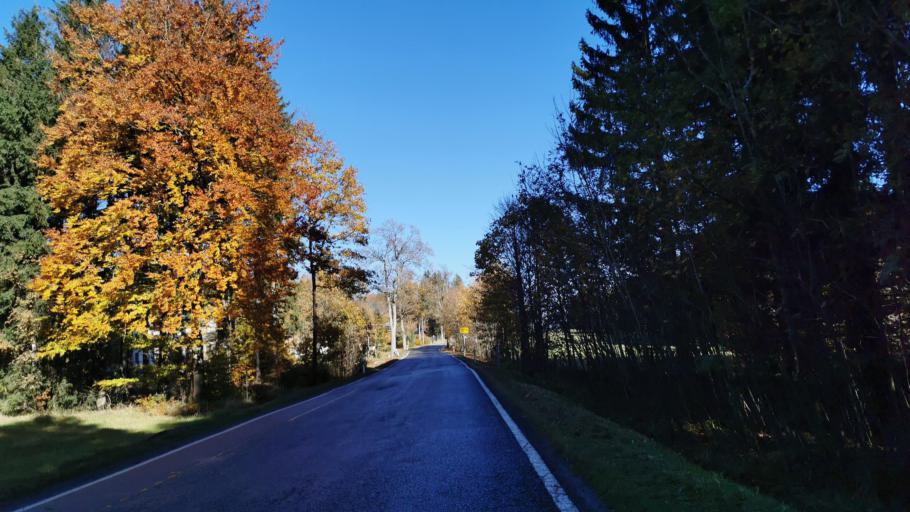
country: DE
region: Bavaria
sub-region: Upper Franconia
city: Nordhalben
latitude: 50.4137
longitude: 11.5282
